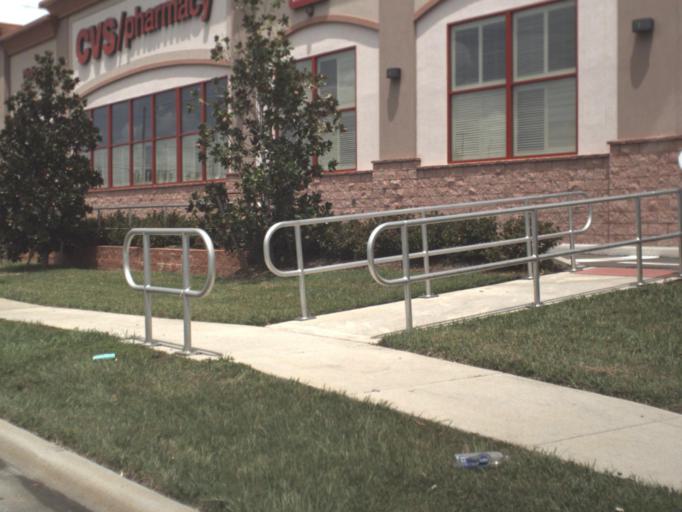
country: US
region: Florida
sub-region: Hillsborough County
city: Town 'n' Country
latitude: 27.9968
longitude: -82.5811
